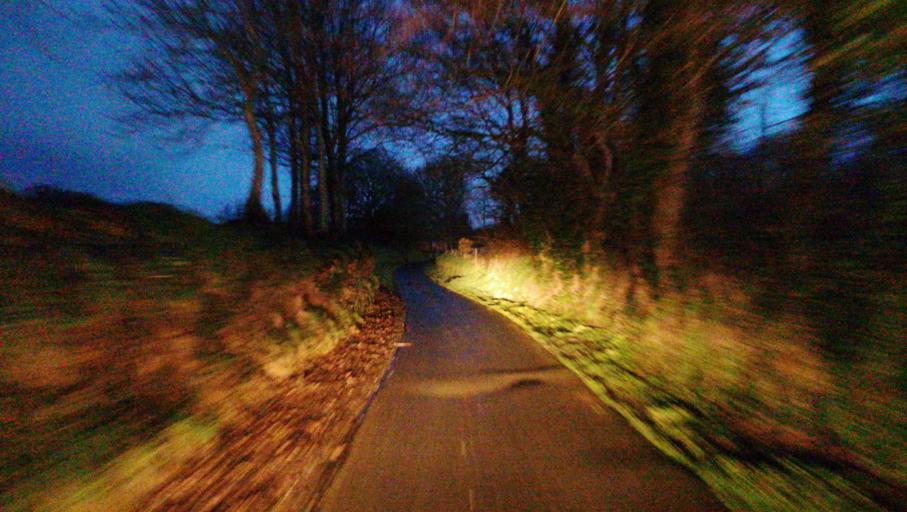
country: FR
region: Brittany
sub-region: Departement des Cotes-d'Armor
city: Plehedel
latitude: 48.6656
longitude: -3.0514
